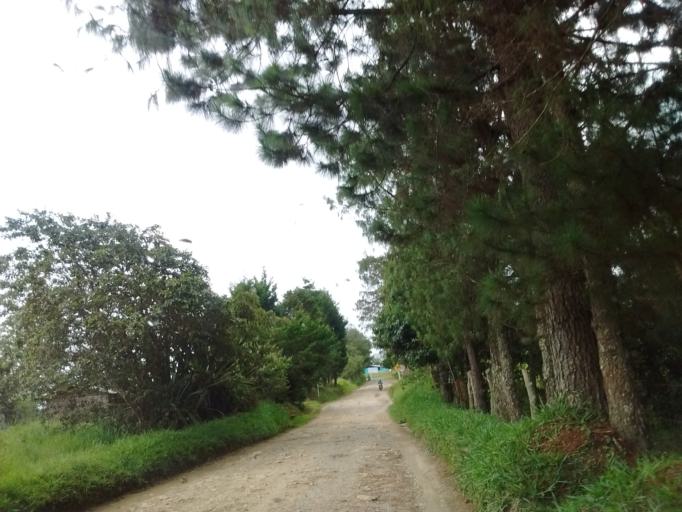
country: CO
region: Cauca
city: Cajibio
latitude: 2.5838
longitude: -76.6753
